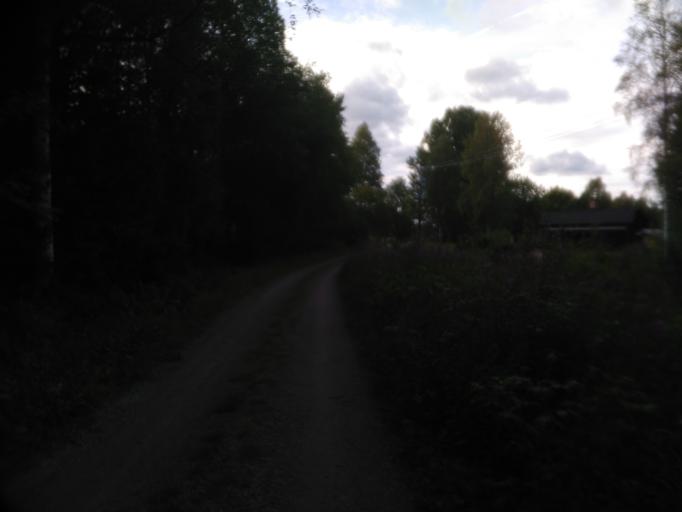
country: SE
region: Dalarna
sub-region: Vansbro Kommun
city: Vansbro
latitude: 60.8318
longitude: 14.2070
